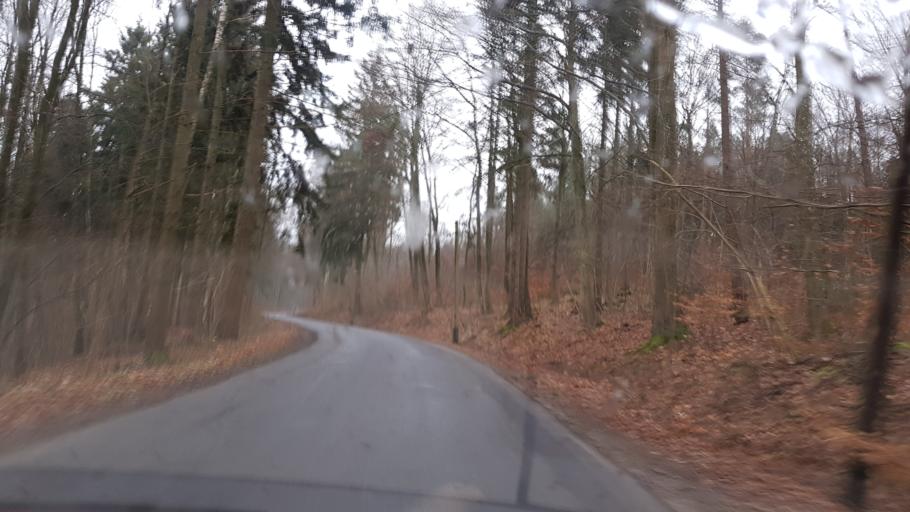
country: PL
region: West Pomeranian Voivodeship
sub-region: Powiat slawienski
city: Slawno
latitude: 54.2640
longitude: 16.5653
